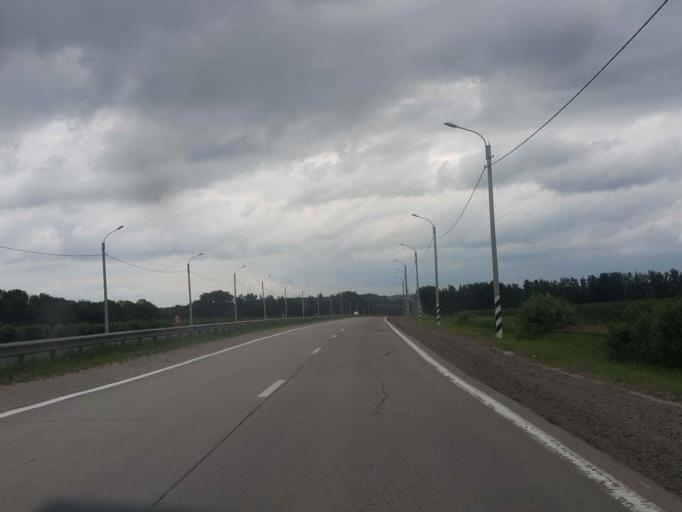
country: RU
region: Tambov
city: Selezni
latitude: 52.7522
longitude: 41.1772
